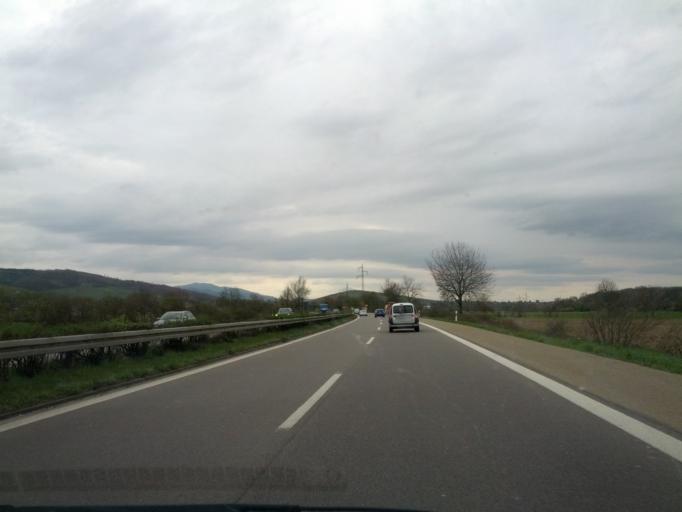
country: DE
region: Baden-Wuerttemberg
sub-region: Freiburg Region
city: Ebringen
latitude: 47.9772
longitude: 7.7737
